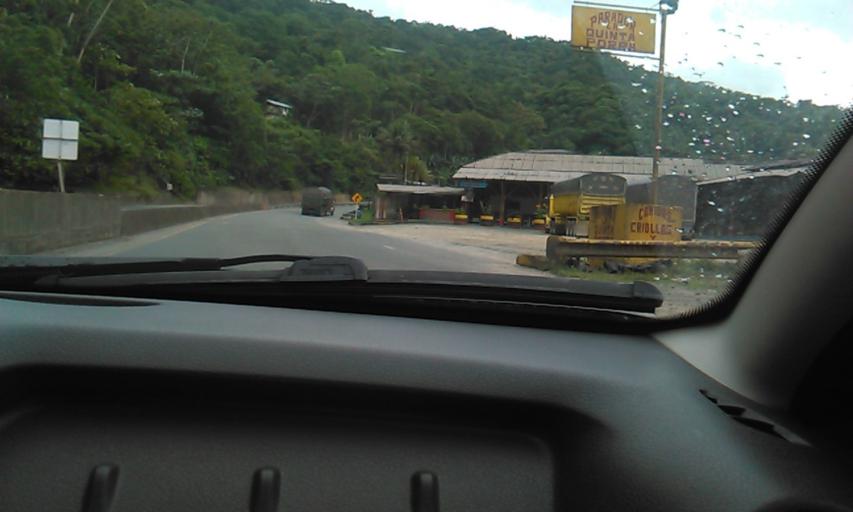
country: CO
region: Valle del Cauca
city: Dagua
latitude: 3.8454
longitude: -76.7949
